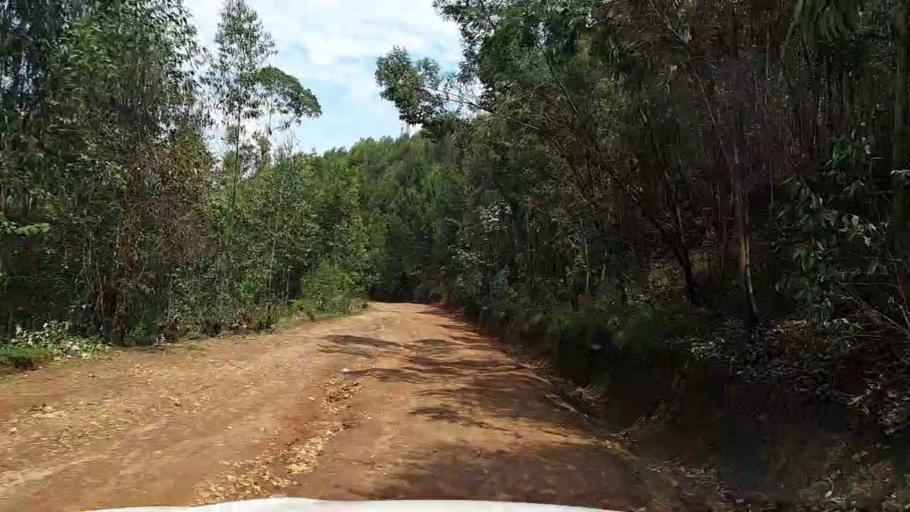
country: RW
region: Southern Province
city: Gikongoro
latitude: -2.3399
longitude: 29.5159
